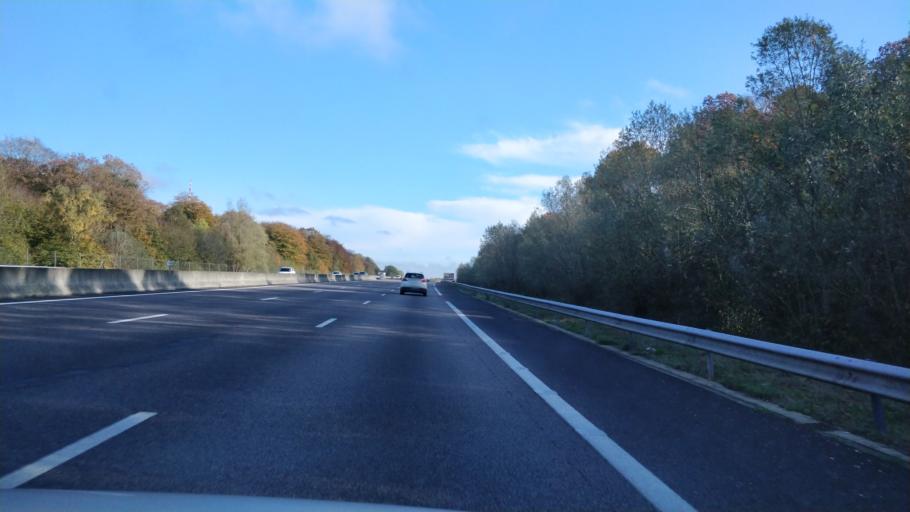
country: FR
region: Haute-Normandie
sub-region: Departement de la Seine-Maritime
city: Grand-Couronne
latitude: 49.3384
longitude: 0.9918
